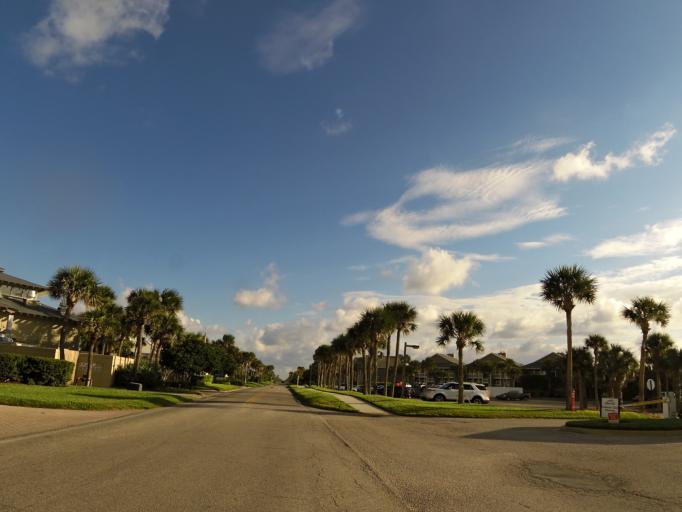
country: US
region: Florida
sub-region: Saint Johns County
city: Sawgrass
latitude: 30.2176
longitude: -81.3719
